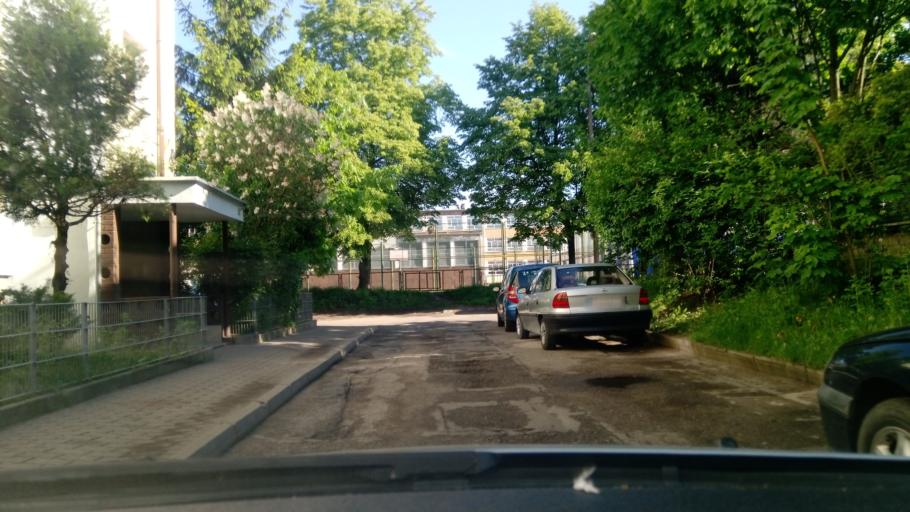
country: PL
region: Lubusz
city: Gorzow Wielkopolski
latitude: 52.7383
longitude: 15.2086
